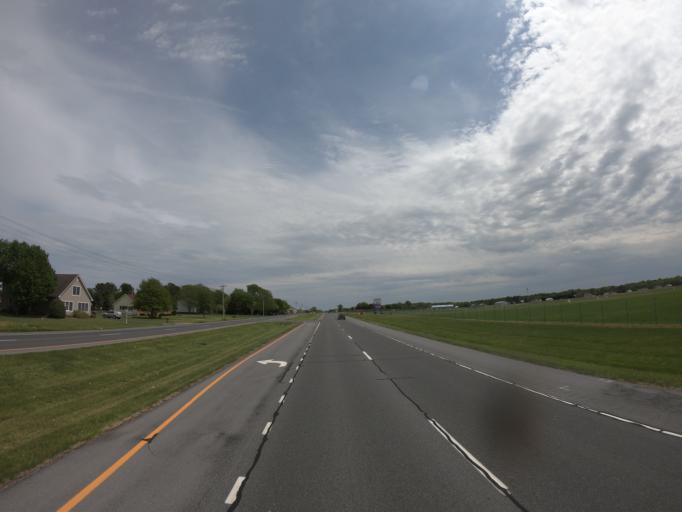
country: US
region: Delaware
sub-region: Sussex County
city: Milton
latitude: 38.7791
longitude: -75.2326
